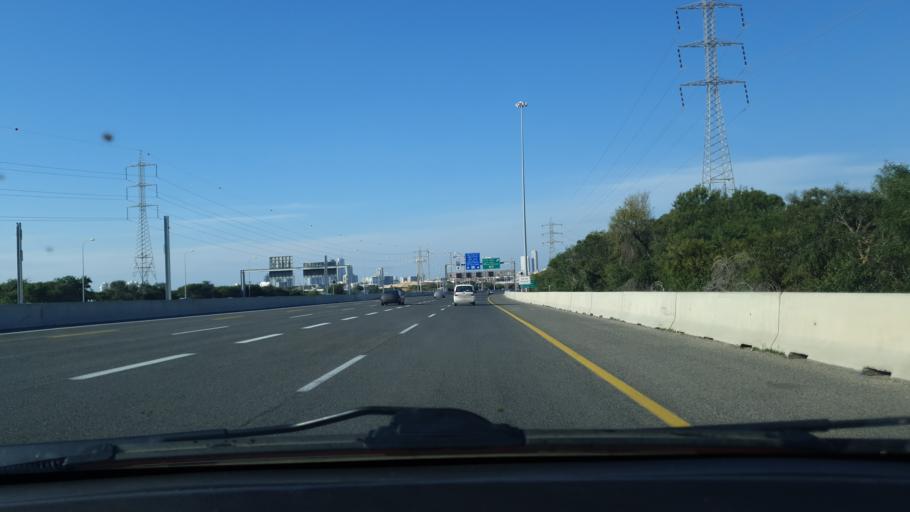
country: IL
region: Central District
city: Rishon LeZiyyon
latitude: 31.9735
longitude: 34.7565
